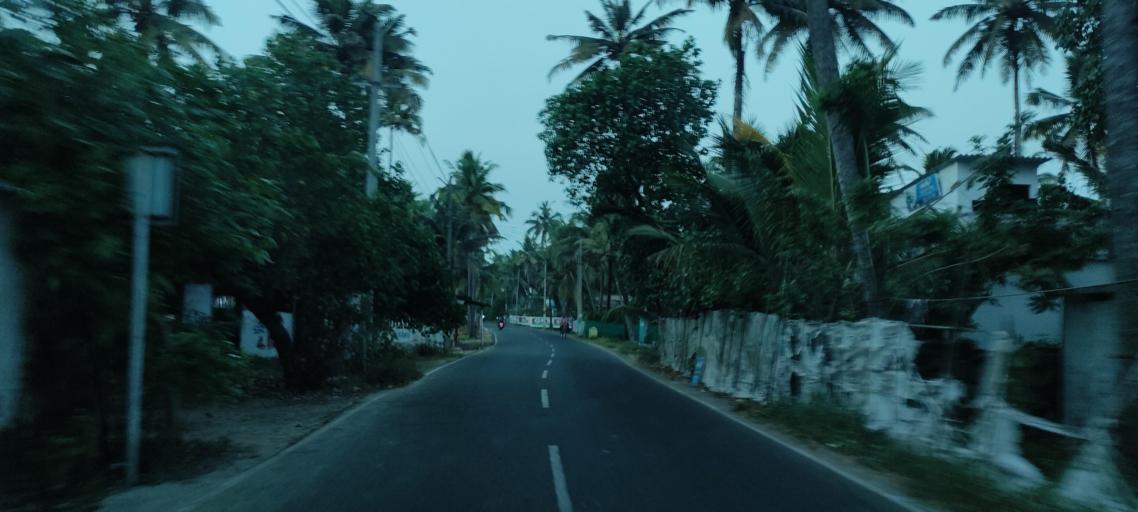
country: IN
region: Kerala
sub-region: Alappuzha
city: Kayankulam
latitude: 9.1199
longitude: 76.4709
